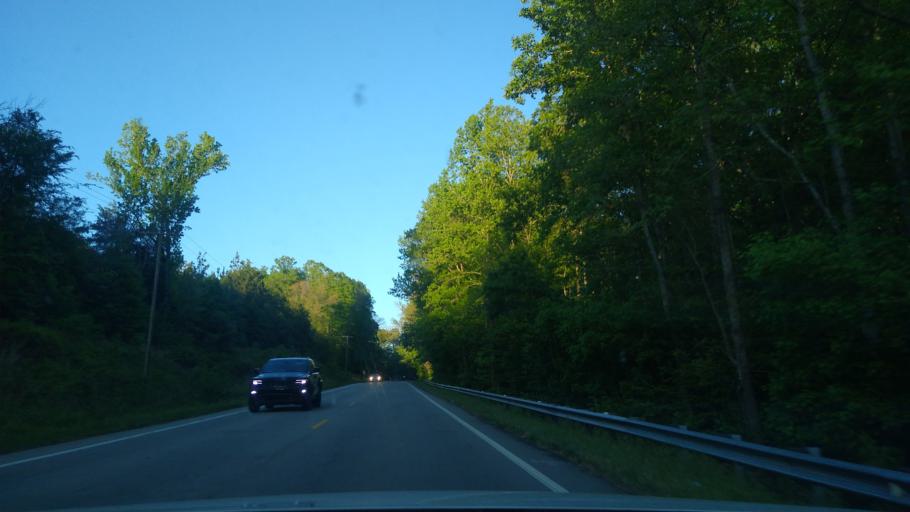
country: US
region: North Carolina
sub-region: Rockingham County
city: Reidsville
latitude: 36.3988
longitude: -79.5271
